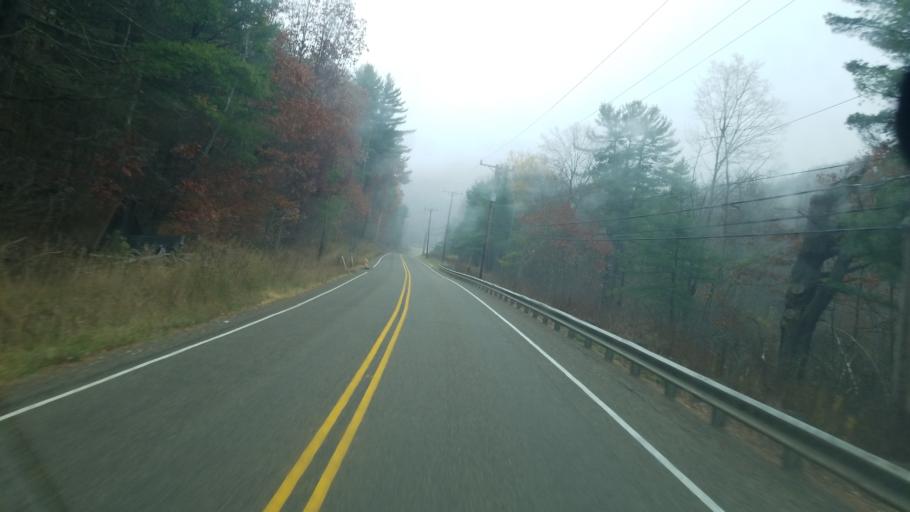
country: US
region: Pennsylvania
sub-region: McKean County
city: Smethport
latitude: 41.8982
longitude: -78.5204
